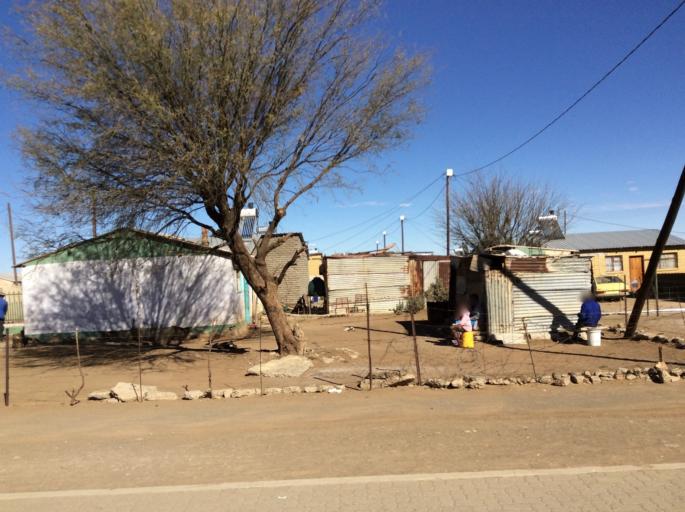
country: ZA
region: Orange Free State
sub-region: Lejweleputswa District Municipality
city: Brandfort
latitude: -28.7337
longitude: 26.1119
